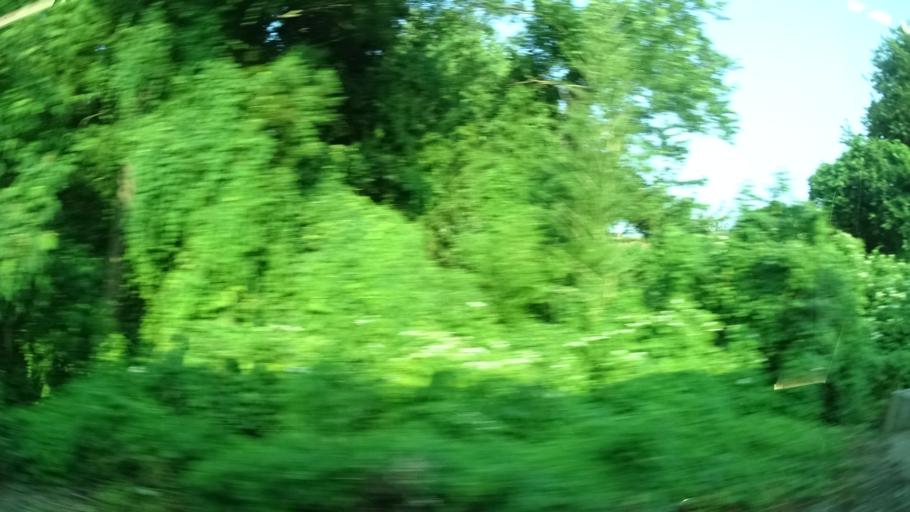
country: JP
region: Ibaraki
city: Hitachi
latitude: 36.6221
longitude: 140.6743
